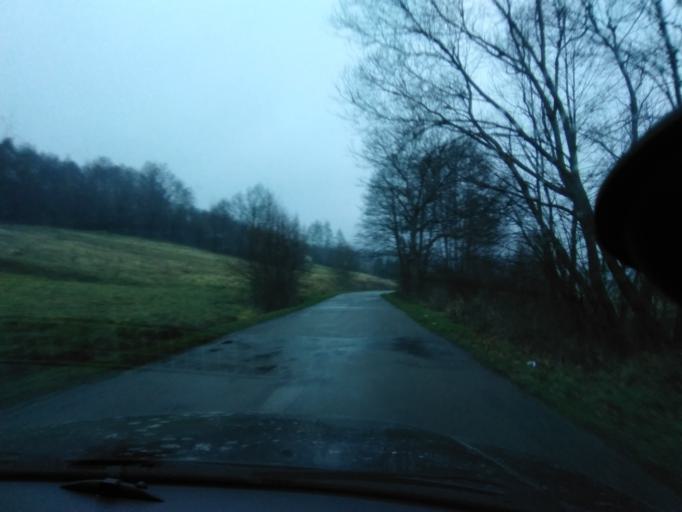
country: PL
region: Subcarpathian Voivodeship
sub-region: Powiat brzozowski
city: Jablonka
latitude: 49.7412
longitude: 22.1482
